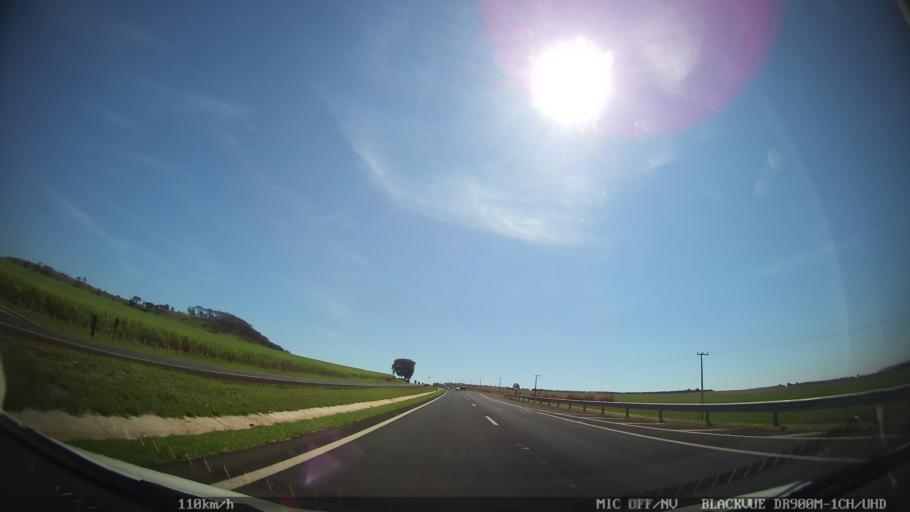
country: BR
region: Sao Paulo
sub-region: Sao Simao
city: Sao Simao
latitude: -21.4335
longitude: -47.6521
